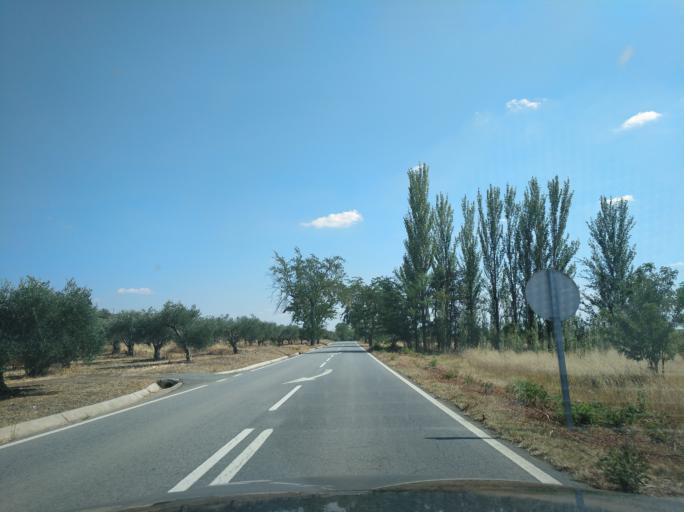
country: PT
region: Portalegre
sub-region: Campo Maior
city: Campo Maior
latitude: 38.9934
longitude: -7.0702
